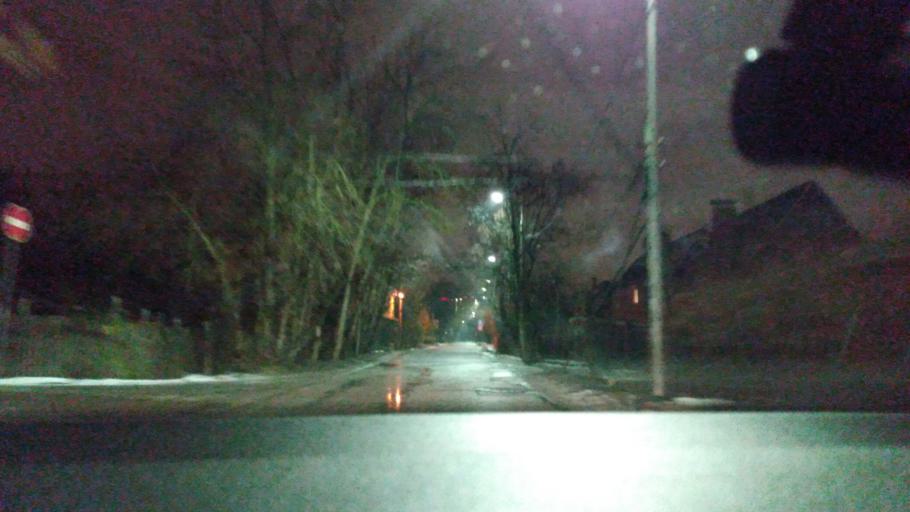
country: RU
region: Moskovskaya
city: Reutov
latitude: 55.7689
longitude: 37.8881
